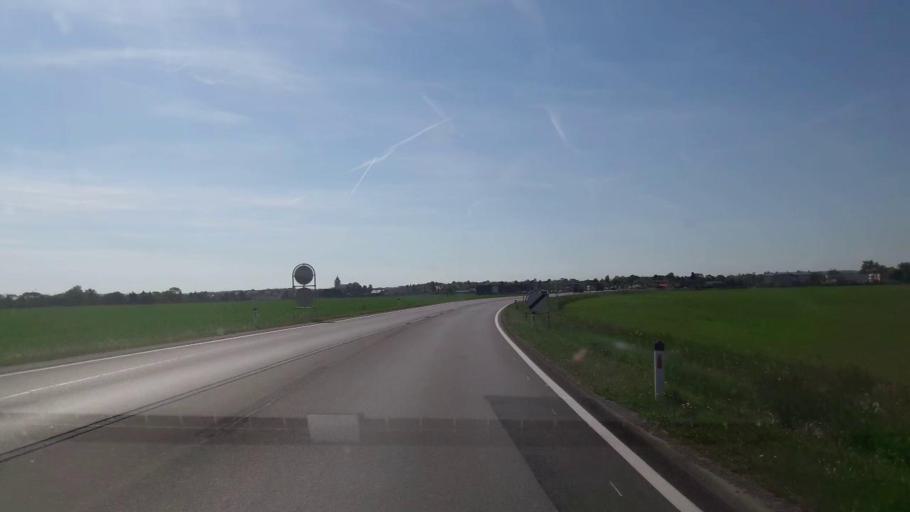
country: AT
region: Burgenland
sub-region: Eisenstadt-Umgebung
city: Trausdorf an der Wulka
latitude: 47.8195
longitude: 16.5431
